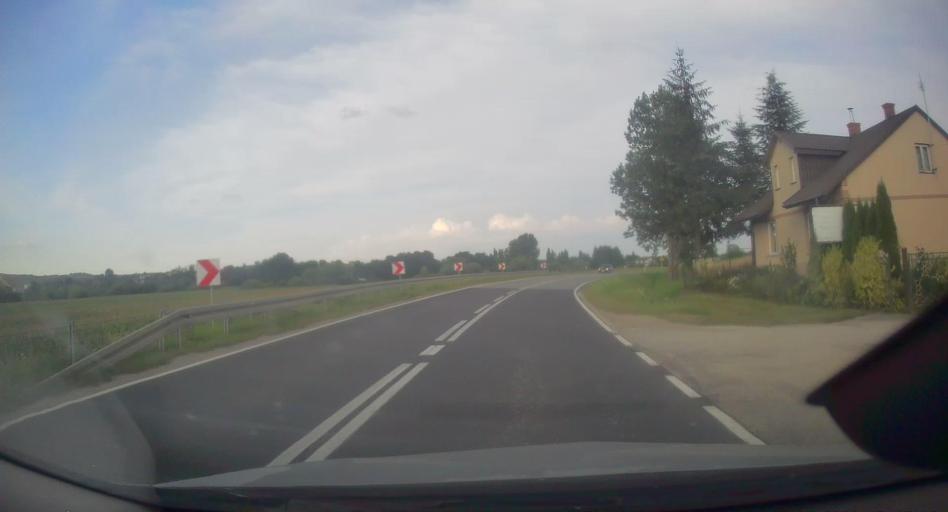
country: PL
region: Lesser Poland Voivodeship
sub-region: Powiat brzeski
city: Szczurowa
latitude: 50.1620
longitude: 20.5665
